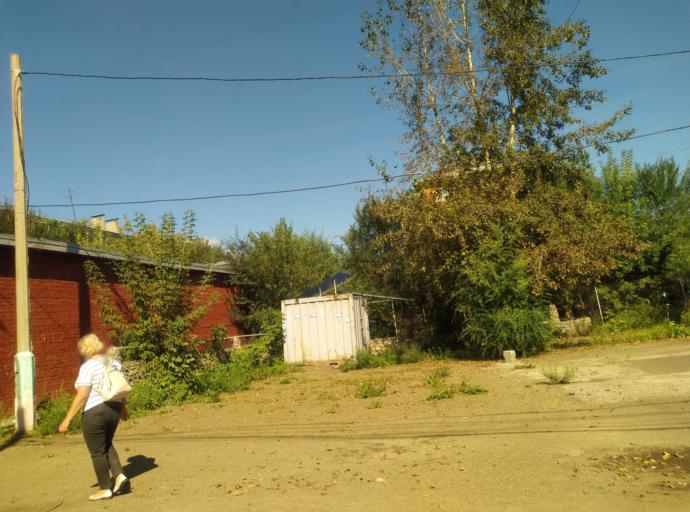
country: RU
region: Krasnoyarskiy
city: Krasnoyarsk
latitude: 55.9787
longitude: 92.8625
